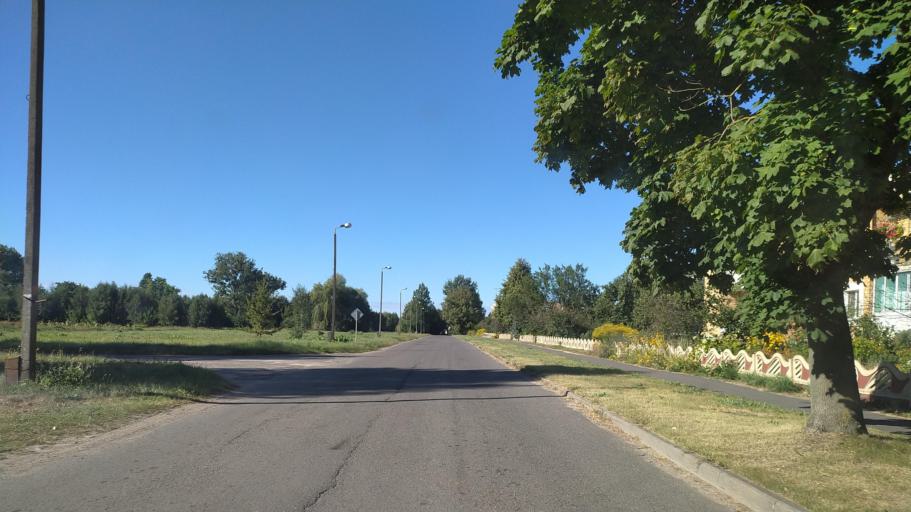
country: BY
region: Brest
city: Pruzhany
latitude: 52.4896
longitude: 24.7127
